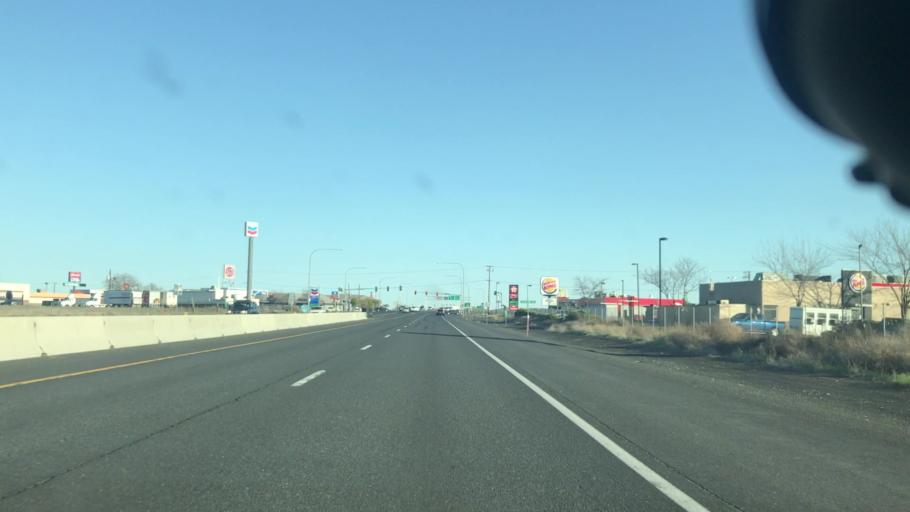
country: US
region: Washington
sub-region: Grant County
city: Moses Lake
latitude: 47.1033
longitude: -119.2486
